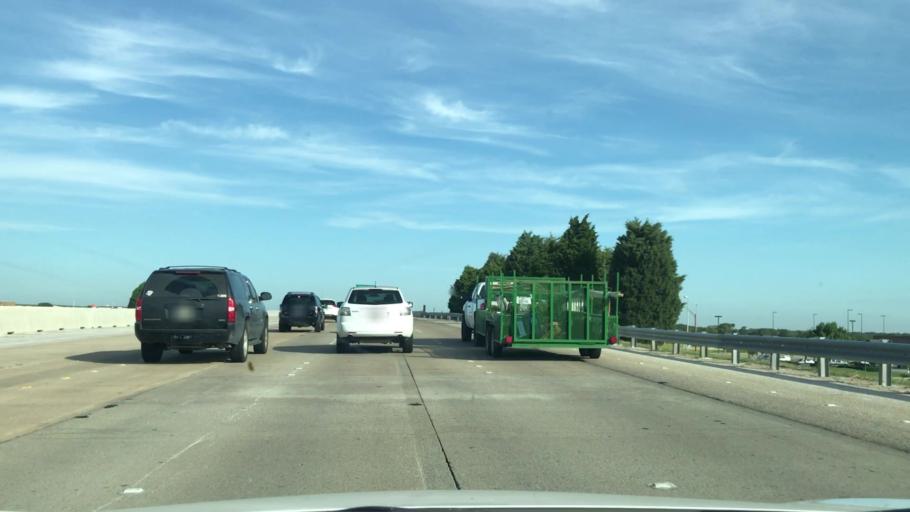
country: US
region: Texas
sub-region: Dallas County
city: Sachse
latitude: 32.9653
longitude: -96.6407
